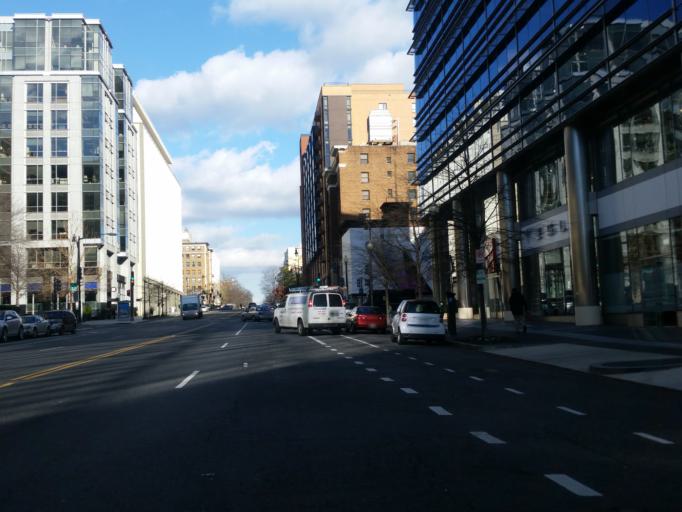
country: US
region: Washington, D.C.
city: Washington, D.C.
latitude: 38.9018
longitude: -77.0271
